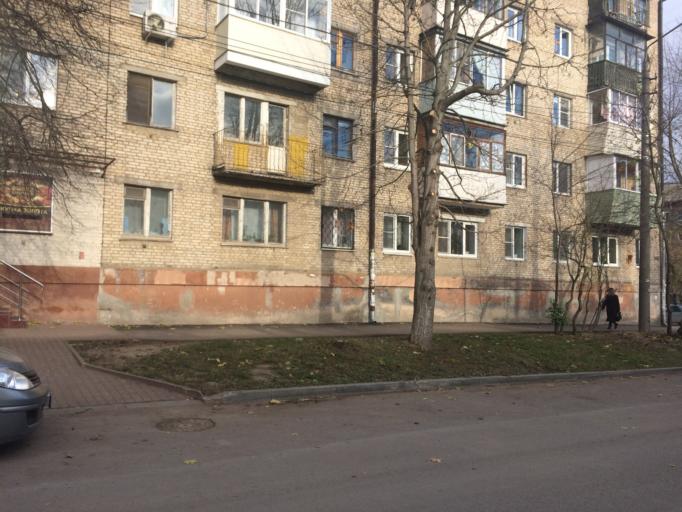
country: RU
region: Tula
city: Mendeleyevskiy
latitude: 54.1624
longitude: 37.5907
